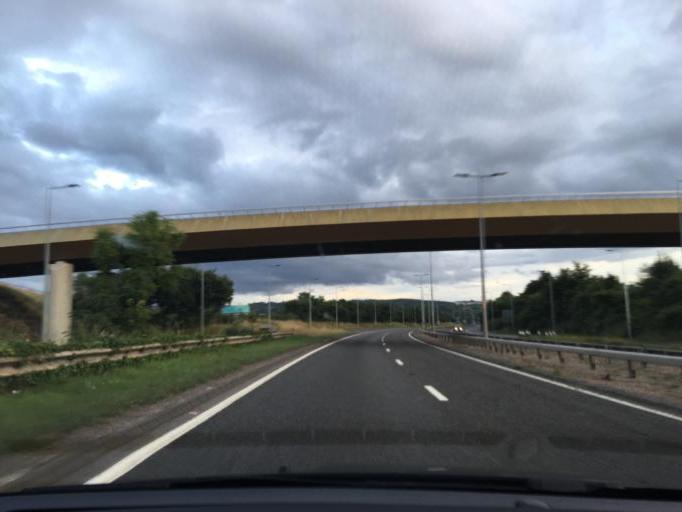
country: GB
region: Scotland
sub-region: Highland
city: Inverness
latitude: 57.4800
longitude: -4.1897
